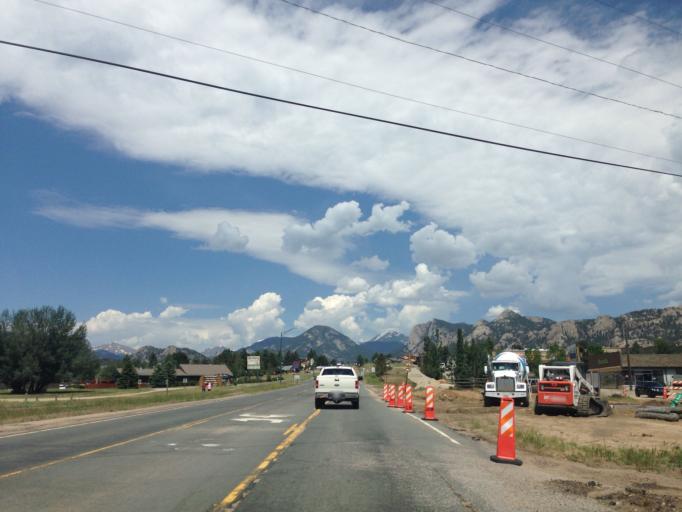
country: US
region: Colorado
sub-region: Larimer County
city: Estes Park
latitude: 40.3794
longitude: -105.4906
